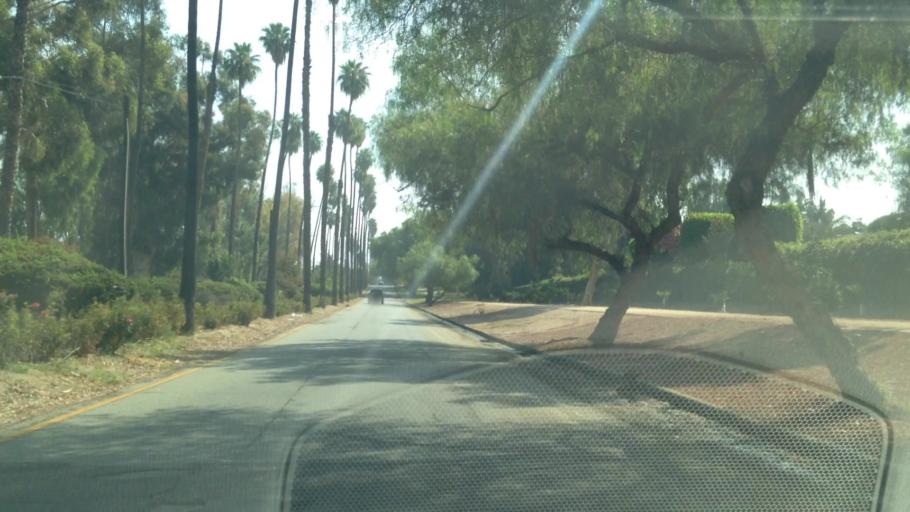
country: US
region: California
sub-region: Riverside County
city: Riverside
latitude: 33.9325
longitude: -117.3847
